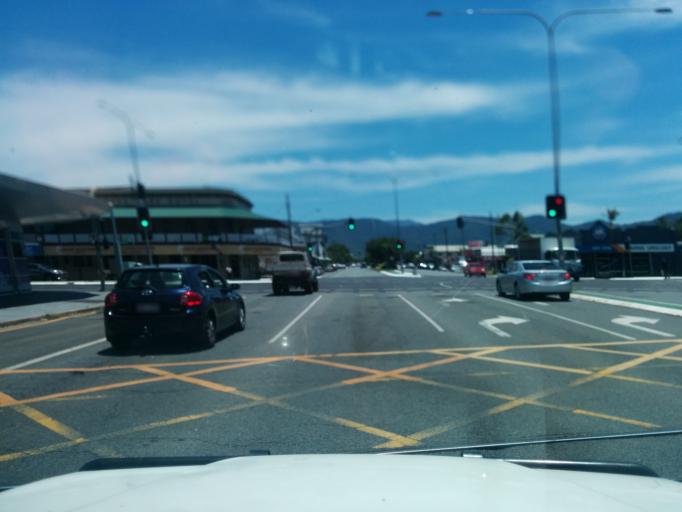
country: AU
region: Queensland
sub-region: Cairns
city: Cairns
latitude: -16.9274
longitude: 145.7728
